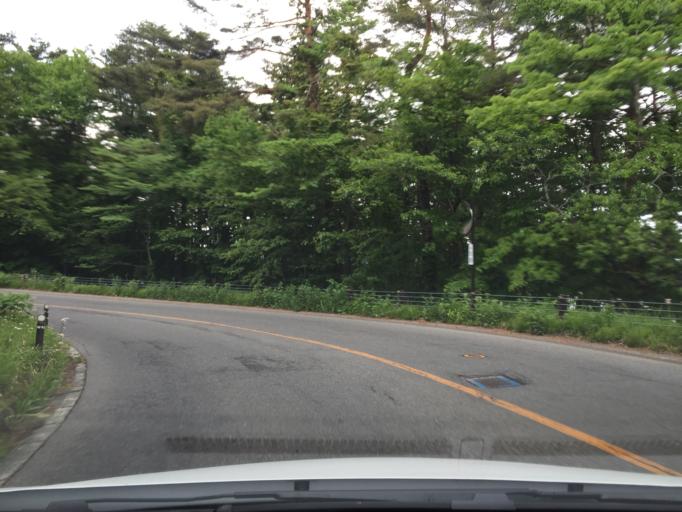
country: JP
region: Fukushima
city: Inawashiro
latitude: 37.6562
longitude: 140.0666
